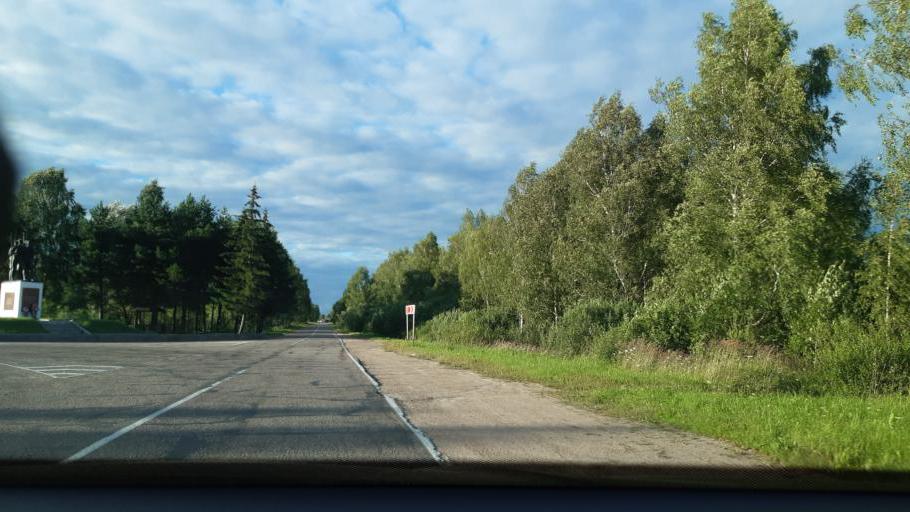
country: RU
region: Smolensk
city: Yel'nya
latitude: 54.5577
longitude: 33.1845
